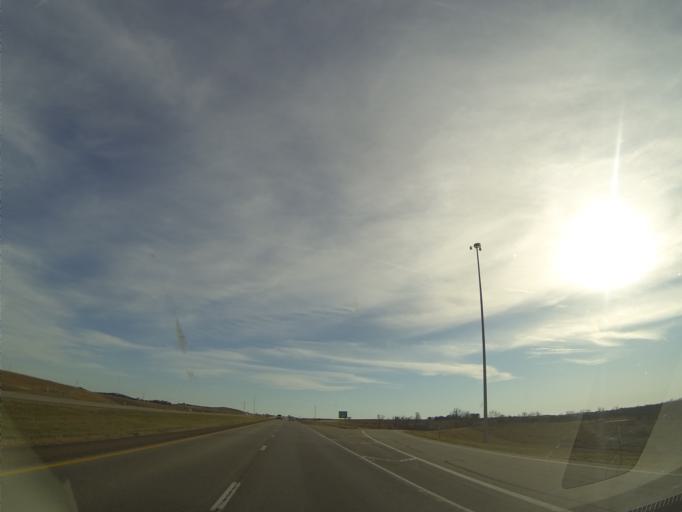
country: US
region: Kansas
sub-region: Ottawa County
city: Minneapolis
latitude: 39.0187
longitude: -97.6421
